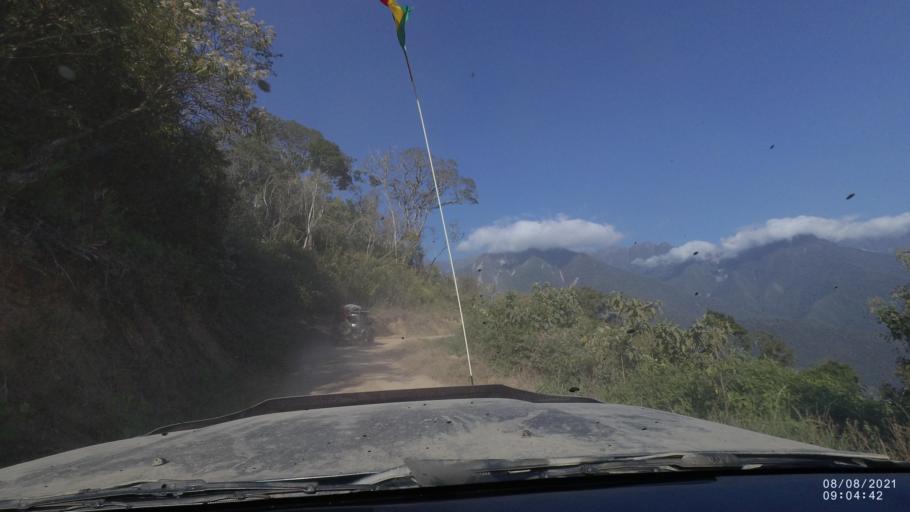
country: BO
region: La Paz
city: Quime
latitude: -16.5557
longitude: -66.7371
